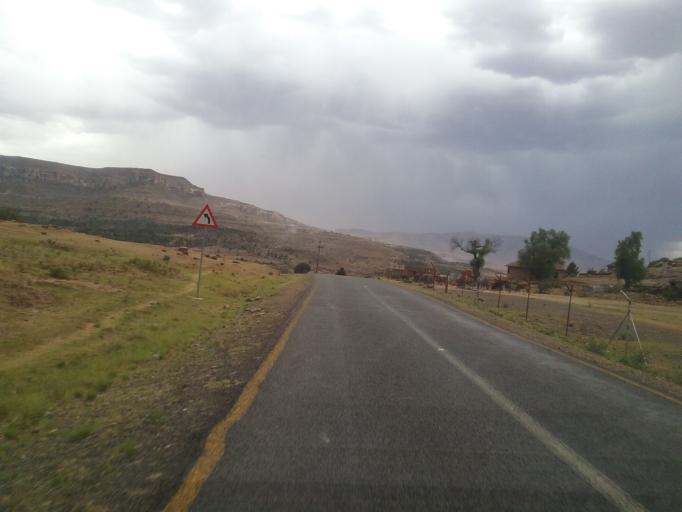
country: LS
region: Quthing
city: Quthing
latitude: -30.2858
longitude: 27.8085
